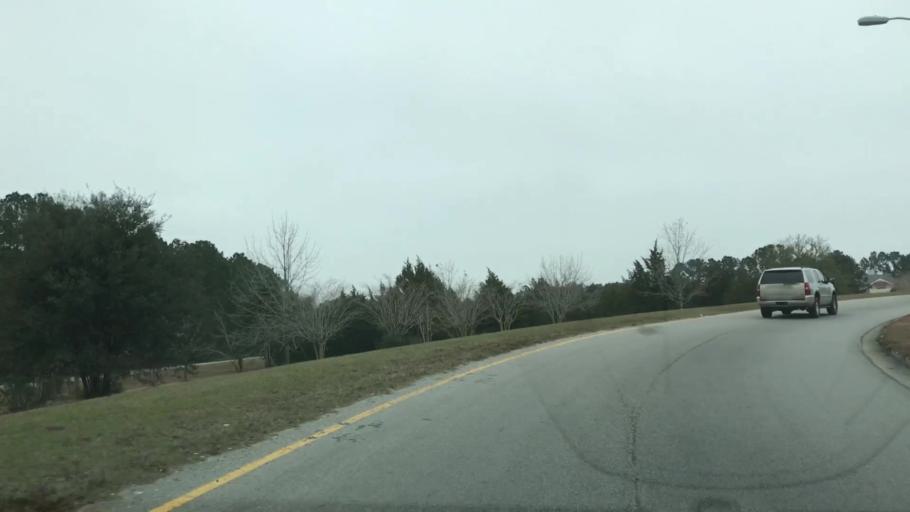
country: US
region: South Carolina
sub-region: Beaufort County
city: Bluffton
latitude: 32.2933
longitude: -80.9386
